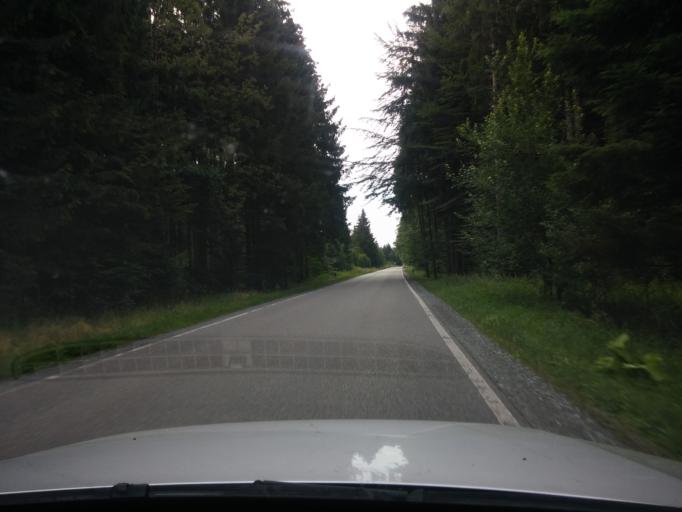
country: DE
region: Bavaria
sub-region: Upper Bavaria
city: Zorneding
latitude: 48.0634
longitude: 11.8194
